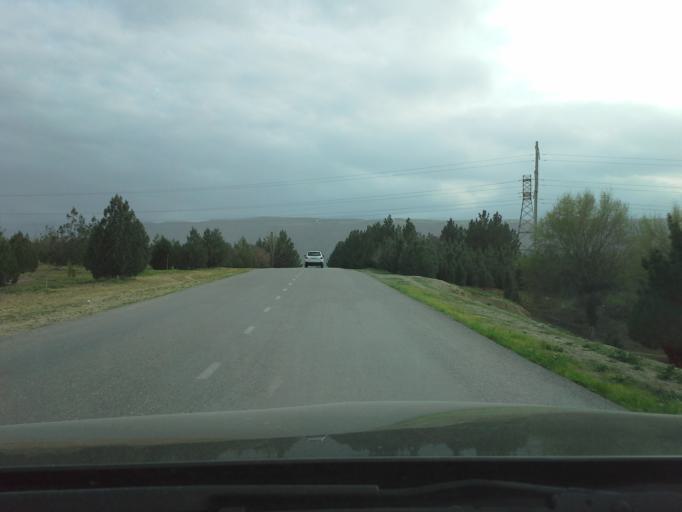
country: TM
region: Ahal
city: Abadan
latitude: 37.9506
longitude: 58.2272
